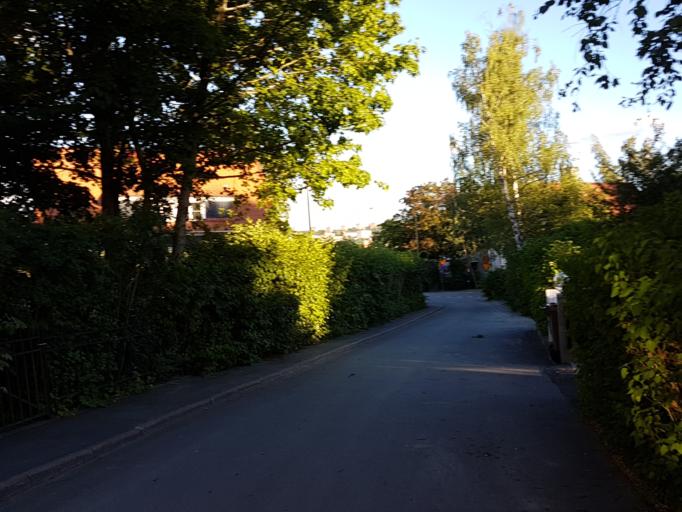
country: SE
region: Stockholm
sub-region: Stockholms Kommun
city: Bromma
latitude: 59.3207
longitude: 17.9693
